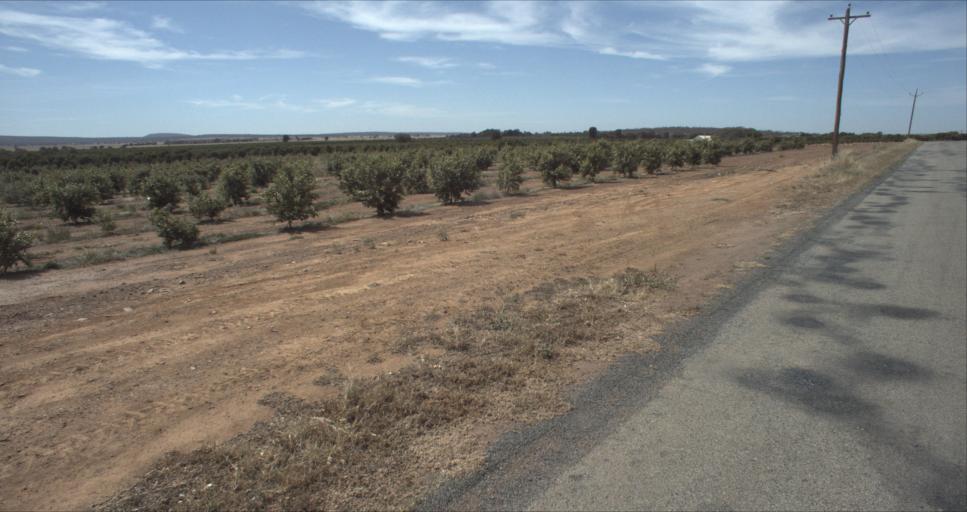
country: AU
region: New South Wales
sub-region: Leeton
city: Leeton
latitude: -34.5668
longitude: 146.4634
